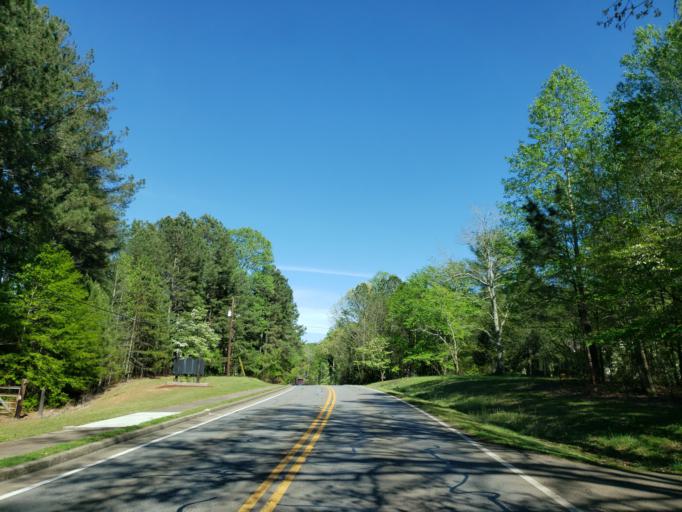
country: US
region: Georgia
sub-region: Cherokee County
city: Canton
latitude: 34.3131
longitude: -84.5454
